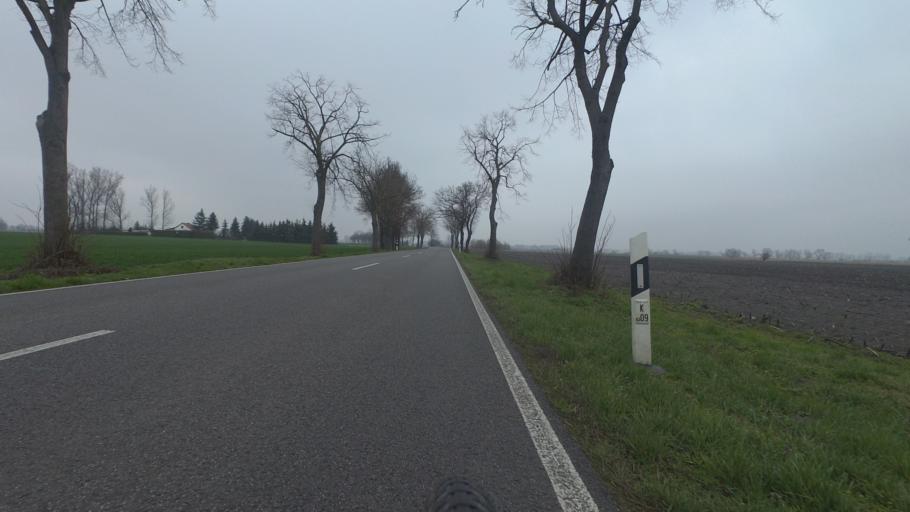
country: DE
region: Brandenburg
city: Nauen
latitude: 52.6226
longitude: 12.8669
